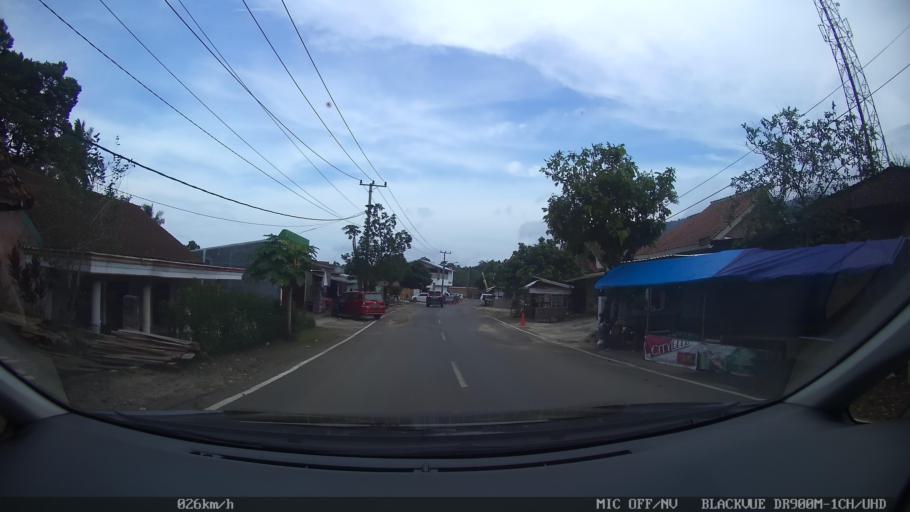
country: ID
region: Lampung
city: Bandarlampung
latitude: -5.4169
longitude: 105.1867
